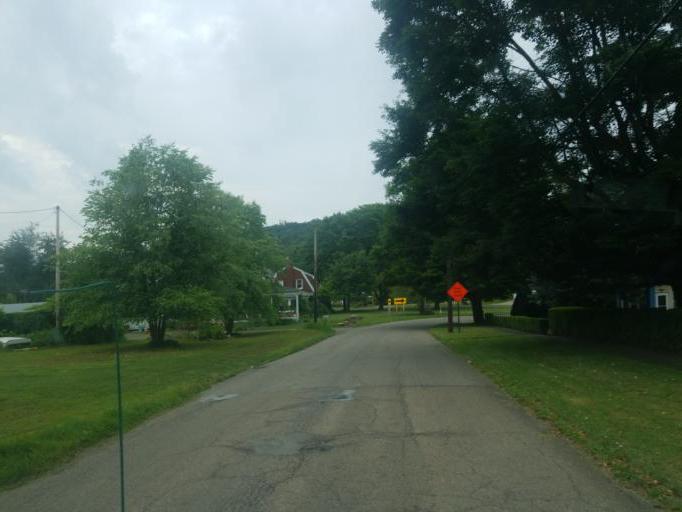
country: US
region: Ohio
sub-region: Carroll County
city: Lake Mohawk
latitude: 40.6690
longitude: -81.2500
